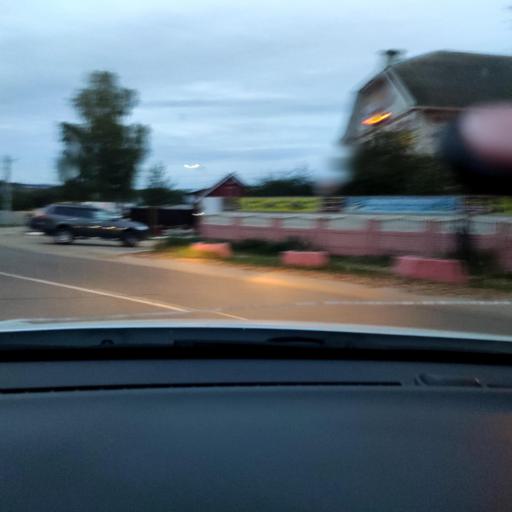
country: RU
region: Mariy-El
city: Volzhsk
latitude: 55.8692
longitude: 48.3693
